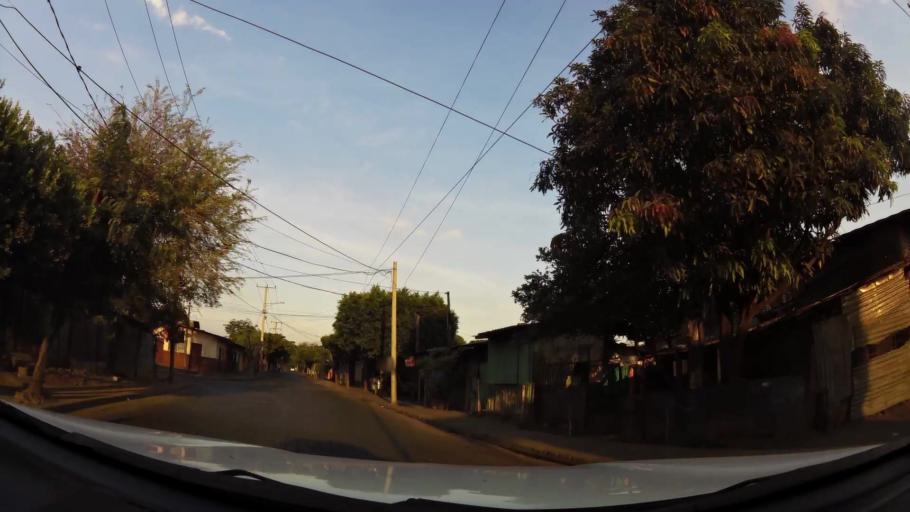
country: NI
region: Managua
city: Managua
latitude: 12.1419
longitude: -86.2557
